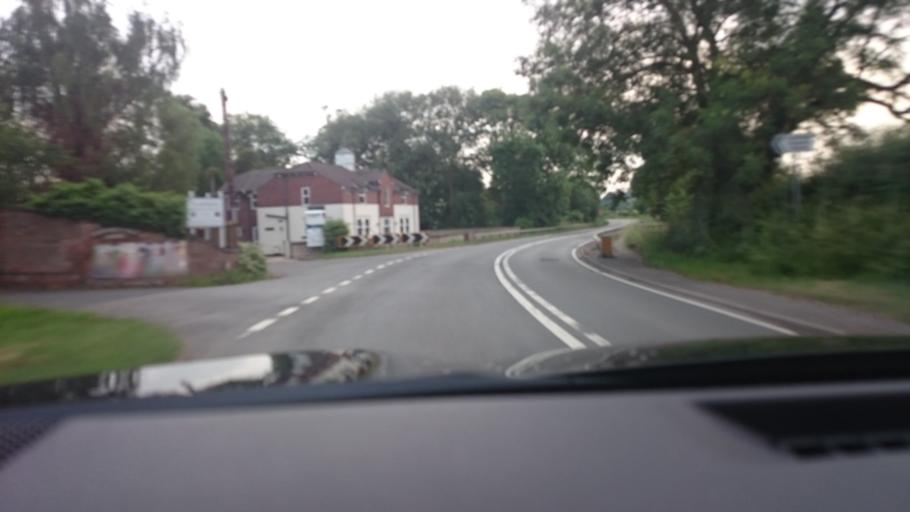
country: GB
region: England
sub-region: Warwickshire
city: Stratford-upon-Avon
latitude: 52.1734
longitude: -1.7125
